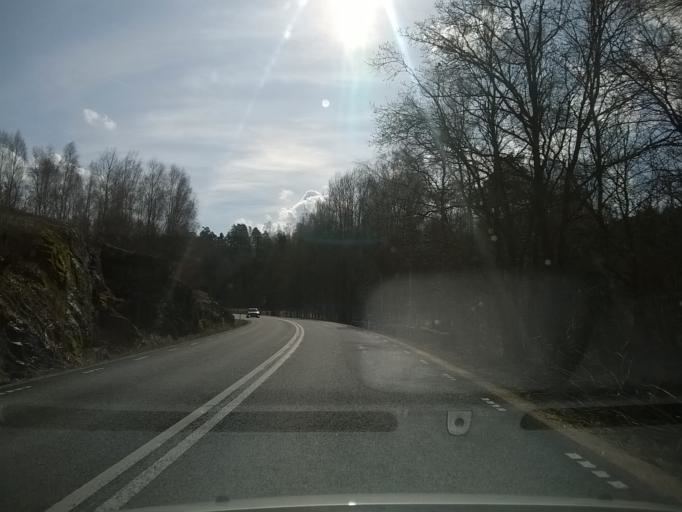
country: SE
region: Vaestra Goetaland
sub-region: Orust
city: Henan
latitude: 58.3210
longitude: 11.6793
